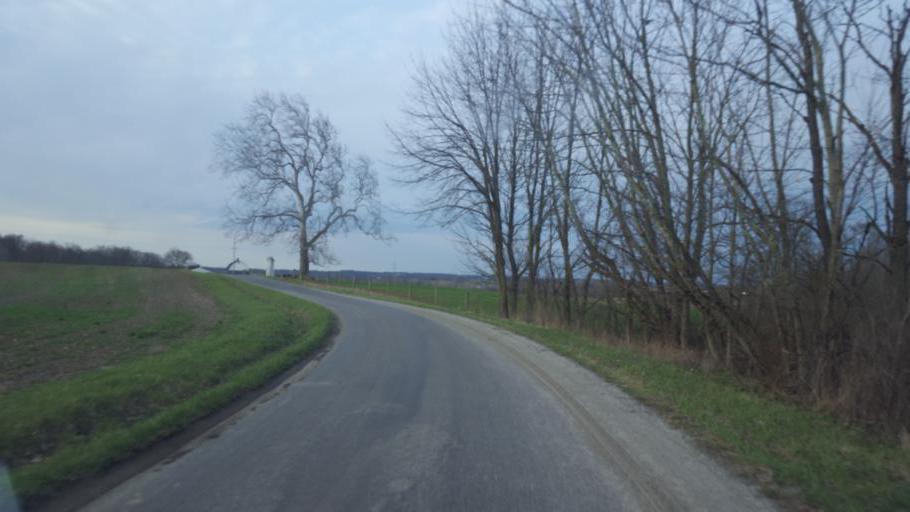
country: US
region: Ohio
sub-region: Knox County
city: Fredericktown
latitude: 40.5482
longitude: -82.5878
